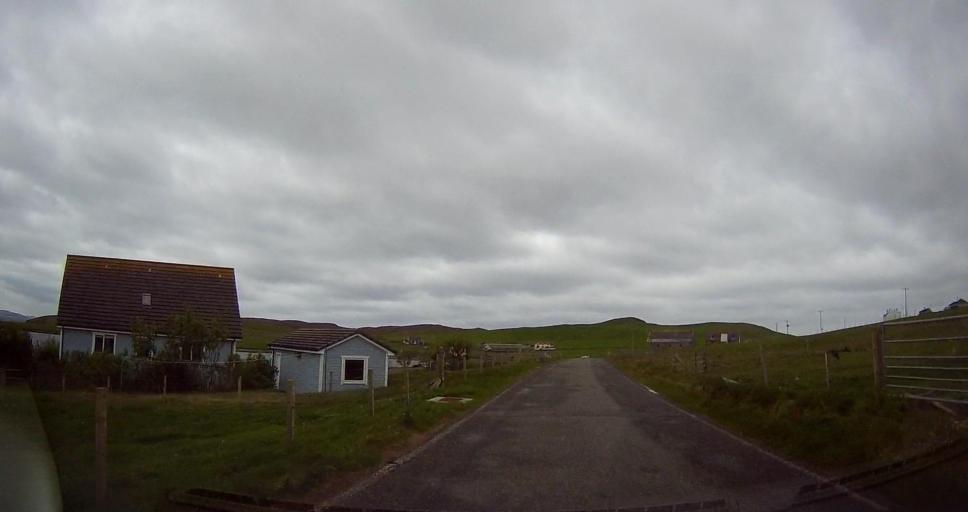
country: GB
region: Scotland
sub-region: Shetland Islands
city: Lerwick
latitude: 60.4783
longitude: -1.4821
